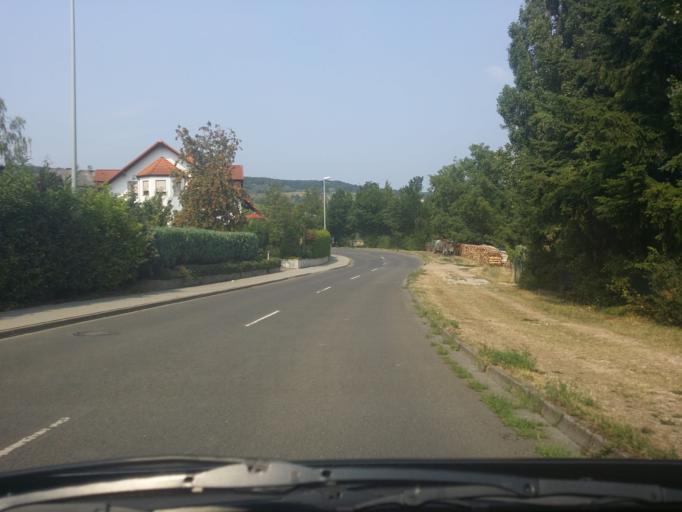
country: DE
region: Rheinland-Pfalz
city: Oestrich-Winkel
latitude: 50.0260
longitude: 8.0370
